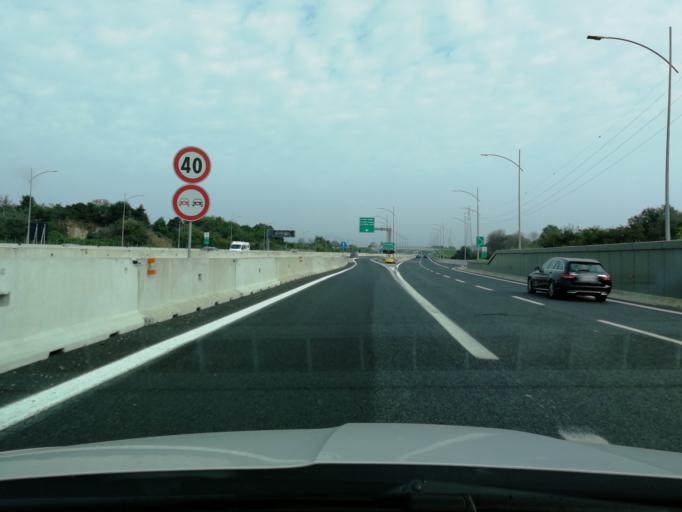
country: IT
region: Latium
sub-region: Citta metropolitana di Roma Capitale
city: Setteville
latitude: 41.9236
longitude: 12.6216
